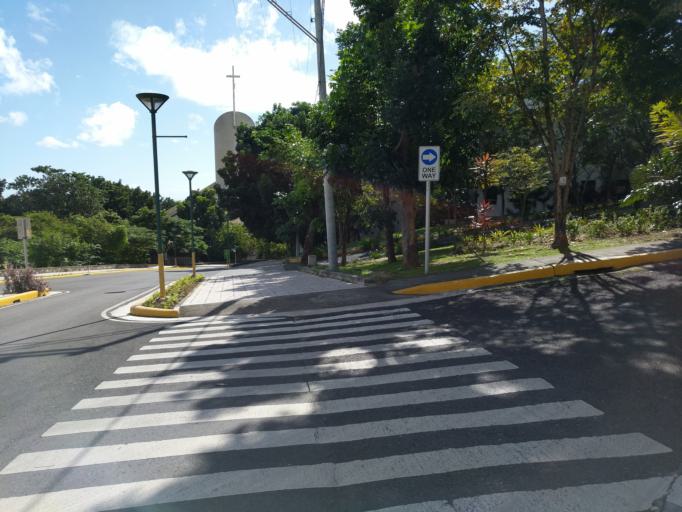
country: PH
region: Central Visayas
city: Mandaue City
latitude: 10.3532
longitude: 123.9104
